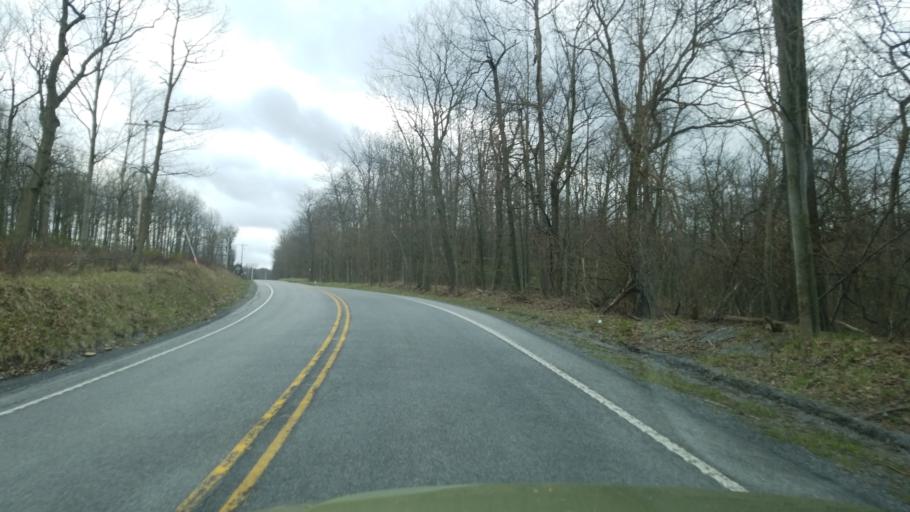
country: US
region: Pennsylvania
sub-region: Blair County
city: Tipton
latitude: 40.7334
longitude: -78.3773
